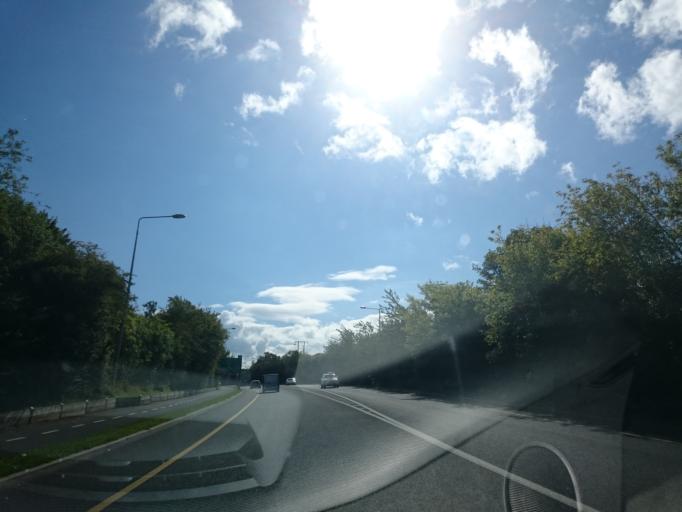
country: IE
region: Leinster
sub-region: Kilkenny
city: Kilkenny
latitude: 52.6371
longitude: -7.2557
